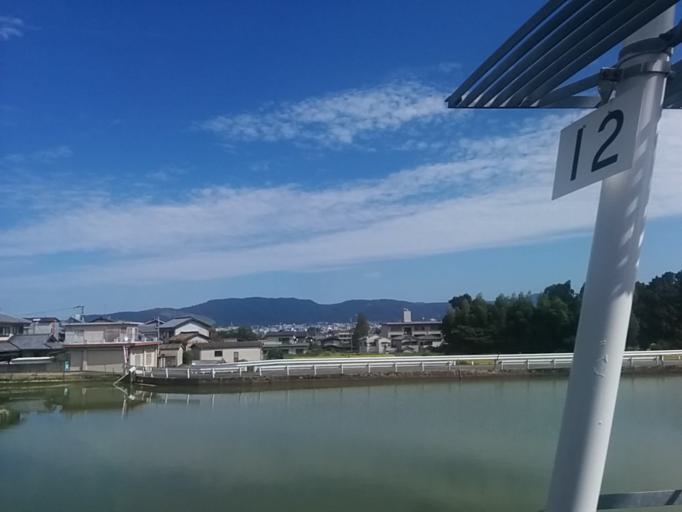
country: JP
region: Nara
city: Nara-shi
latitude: 34.6798
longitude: 135.7837
